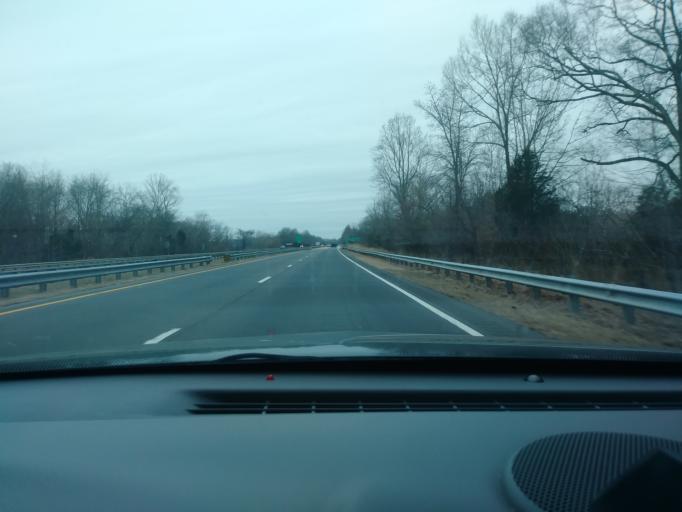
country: US
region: North Carolina
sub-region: Forsyth County
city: Lewisville
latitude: 36.1029
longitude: -80.5056
